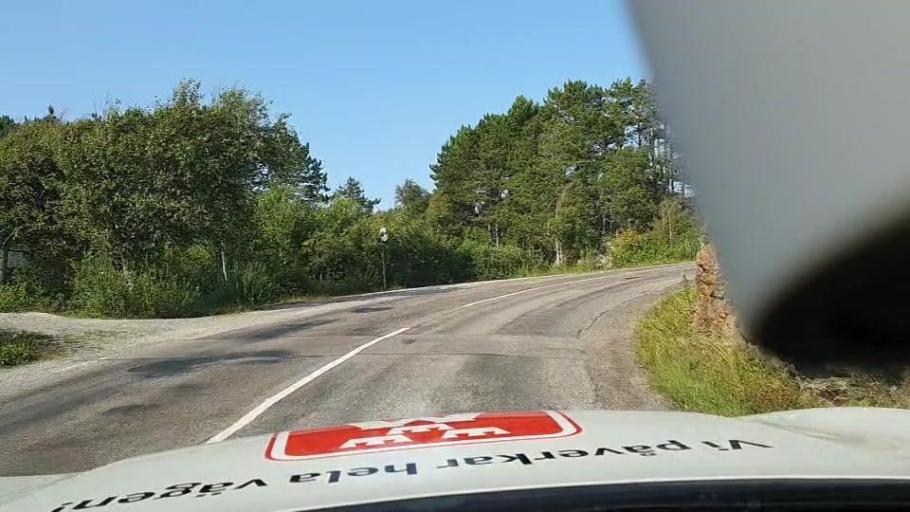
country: SE
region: Vaestra Goetaland
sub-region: Tjorns Kommun
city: Skaerhamn
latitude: 58.0785
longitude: 11.4815
